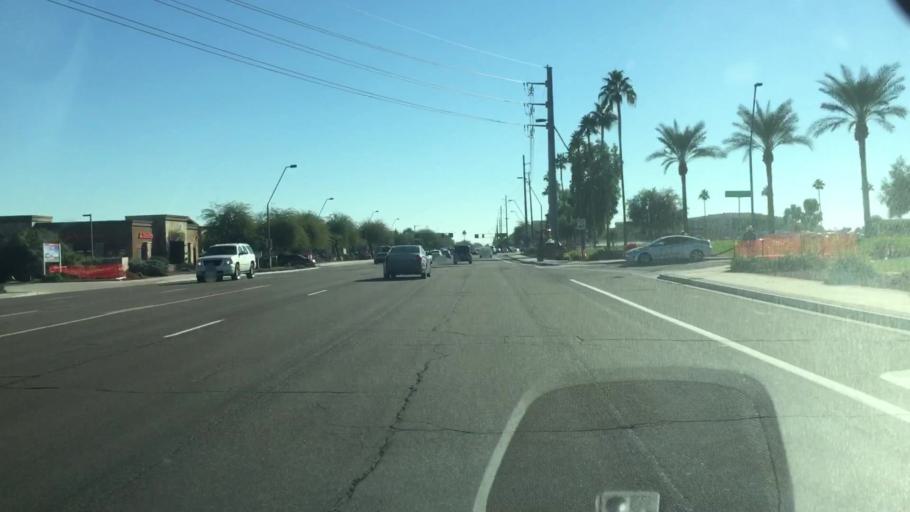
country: US
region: Arizona
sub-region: Maricopa County
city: Guadalupe
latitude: 33.3372
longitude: -111.9632
